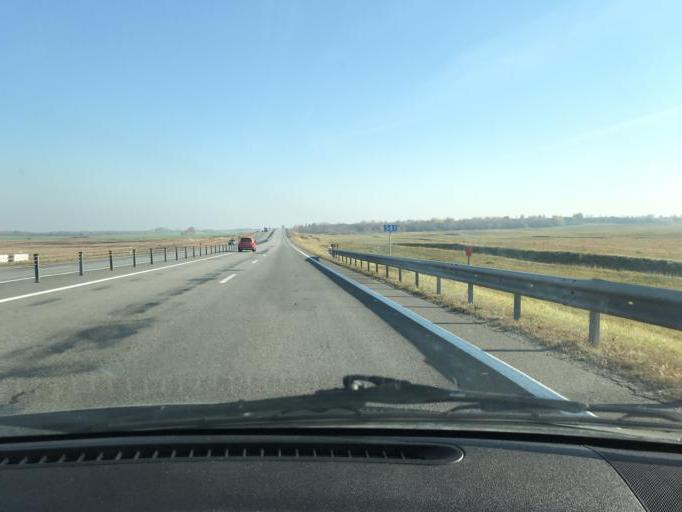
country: BY
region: Vitebsk
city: Dubrowna
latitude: 54.6372
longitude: 30.5478
